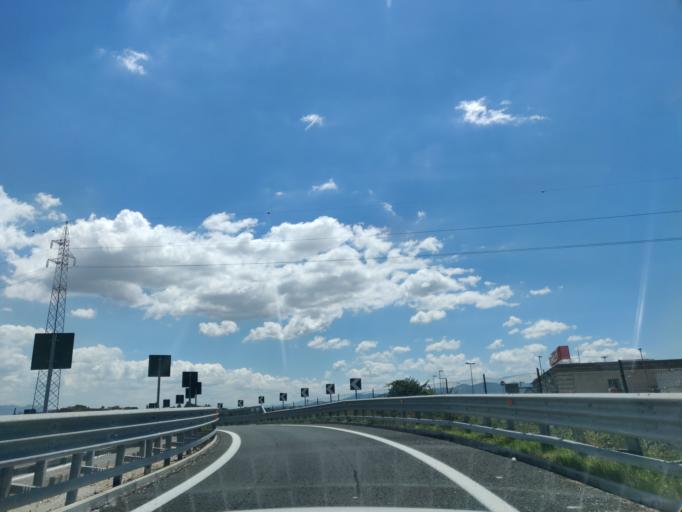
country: IT
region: Latium
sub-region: Citta metropolitana di Roma Capitale
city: Setteville
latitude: 41.9176
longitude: 12.6616
